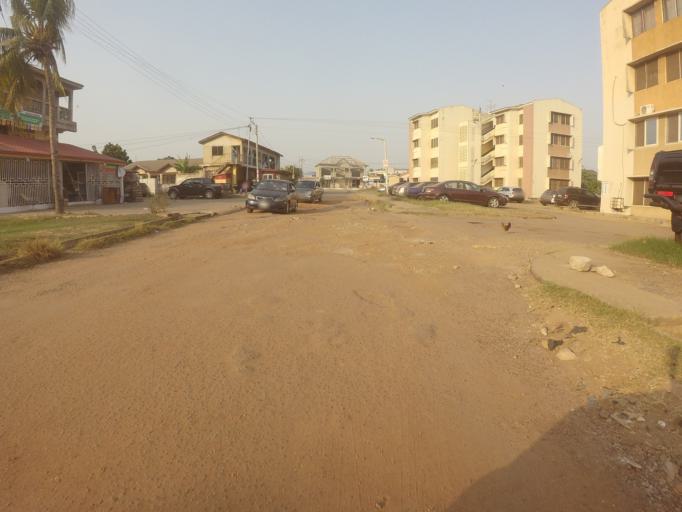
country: GH
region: Greater Accra
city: Nungua
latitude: 5.6252
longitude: -0.0636
